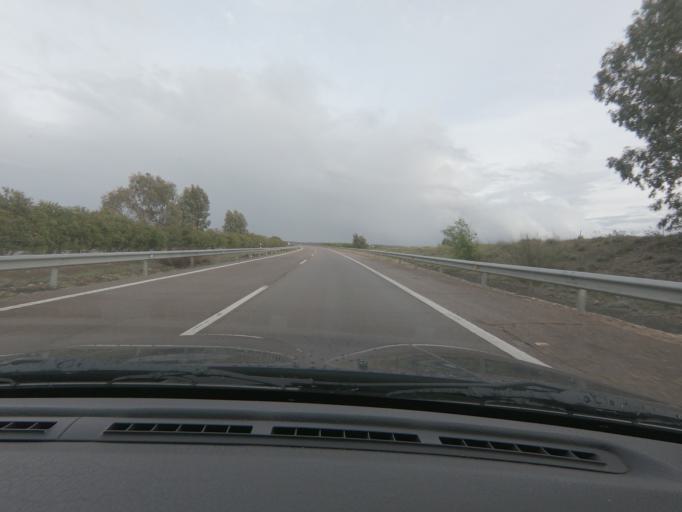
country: ES
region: Extremadura
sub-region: Provincia de Badajoz
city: Badajoz
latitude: 38.9122
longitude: -6.9488
